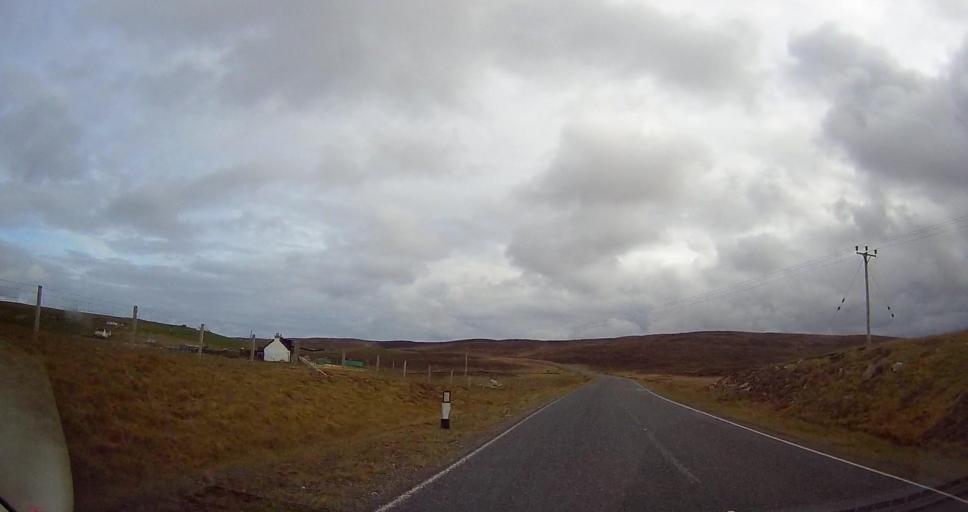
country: GB
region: Scotland
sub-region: Shetland Islands
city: Shetland
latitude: 60.5678
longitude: -1.1772
